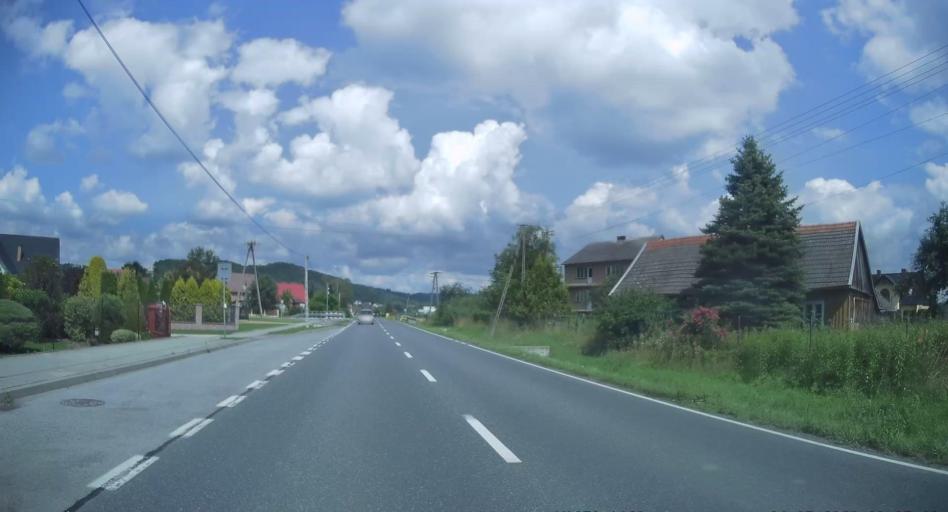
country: PL
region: Lesser Poland Voivodeship
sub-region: Powiat tarnowski
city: Janowice
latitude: 49.8886
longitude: 20.8256
